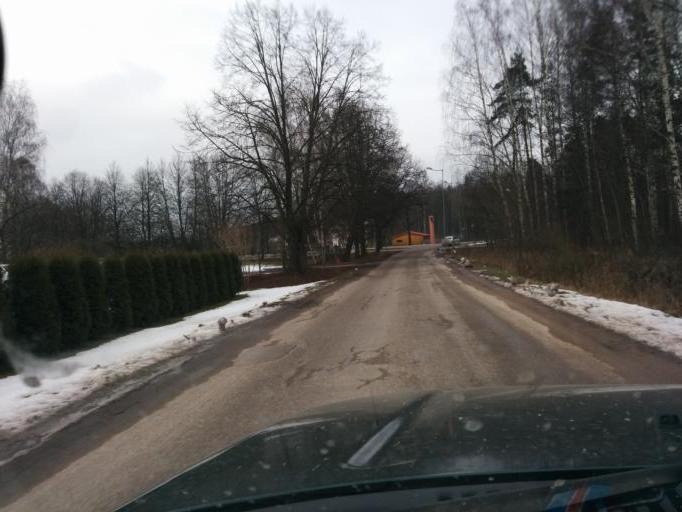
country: LV
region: Ozolnieku
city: Ozolnieki
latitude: 56.6827
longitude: 23.7805
